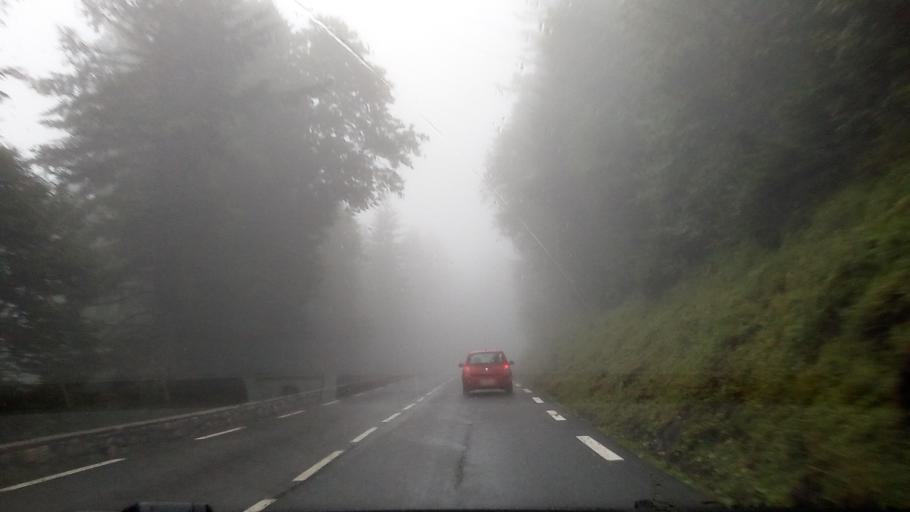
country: FR
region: Midi-Pyrenees
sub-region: Departement des Hautes-Pyrenees
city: Campan
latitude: 42.9223
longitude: 0.1991
